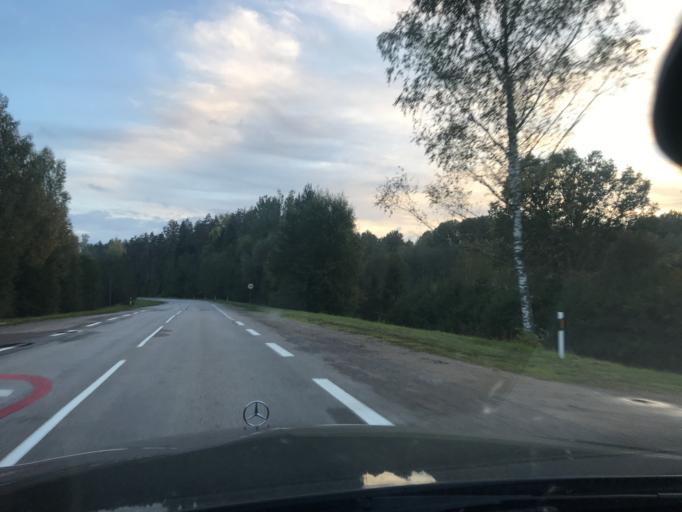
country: EE
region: Valgamaa
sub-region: Torva linn
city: Torva
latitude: 58.0043
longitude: 26.0820
